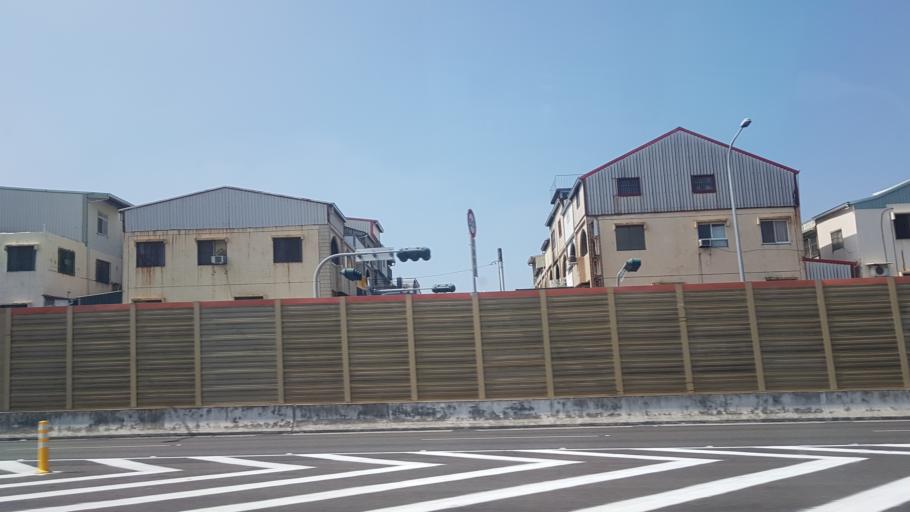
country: TW
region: Taiwan
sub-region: Tainan
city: Tainan
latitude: 23.0030
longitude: 120.2480
